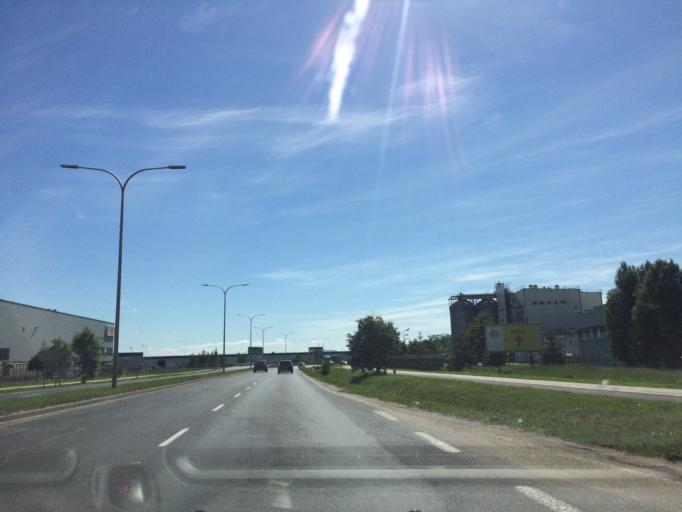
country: PL
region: Lower Silesian Voivodeship
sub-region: Powiat wroclawski
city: Bielany Wroclawskie
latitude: 51.0440
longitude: 16.9525
